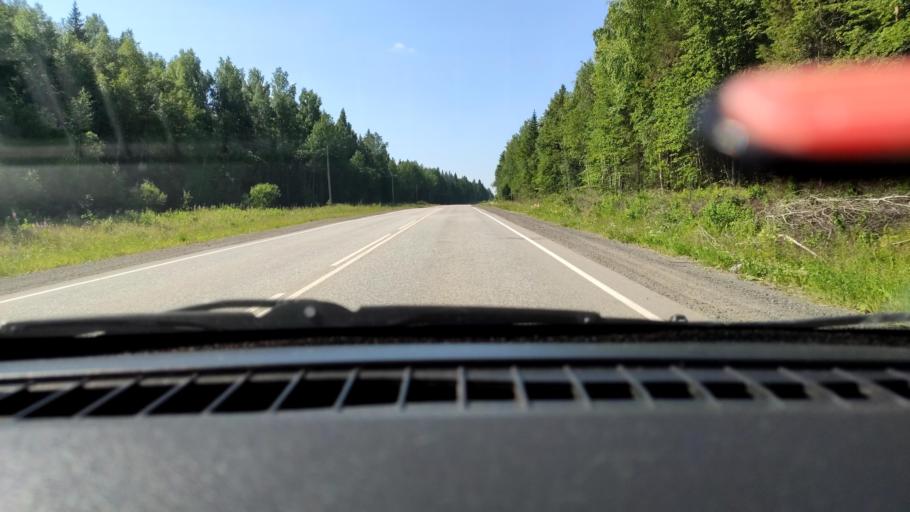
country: RU
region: Perm
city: Kultayevo
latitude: 57.7917
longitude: 55.7759
